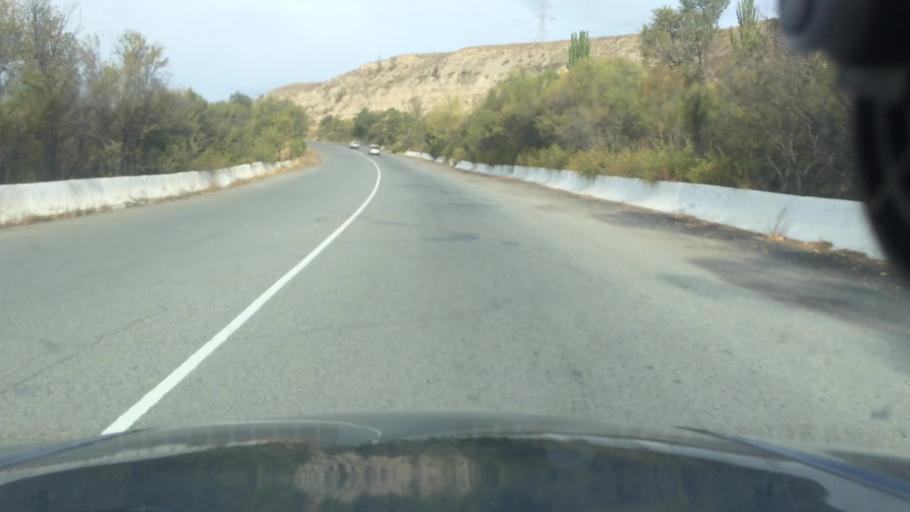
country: KG
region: Ysyk-Koel
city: Karakol
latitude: 42.5943
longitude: 78.3851
